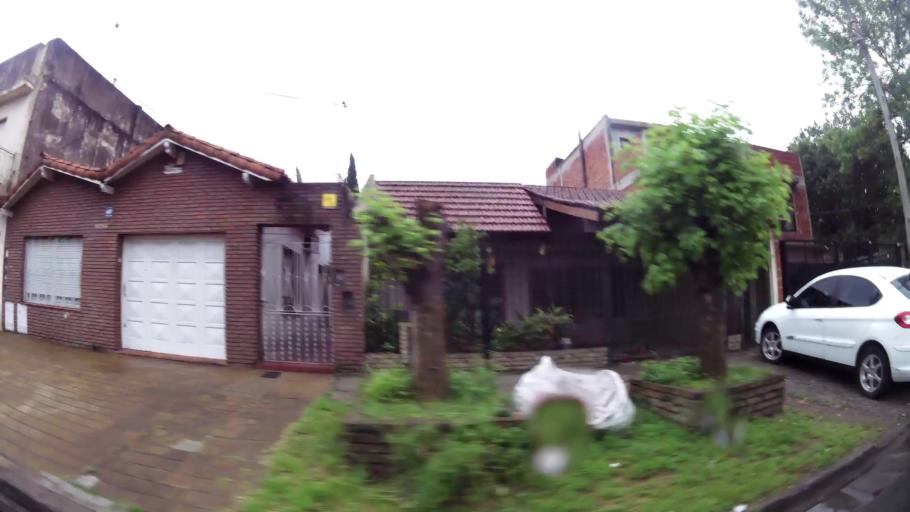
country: AR
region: Buenos Aires
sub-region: Partido de Lomas de Zamora
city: Lomas de Zamora
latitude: -34.7433
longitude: -58.3756
